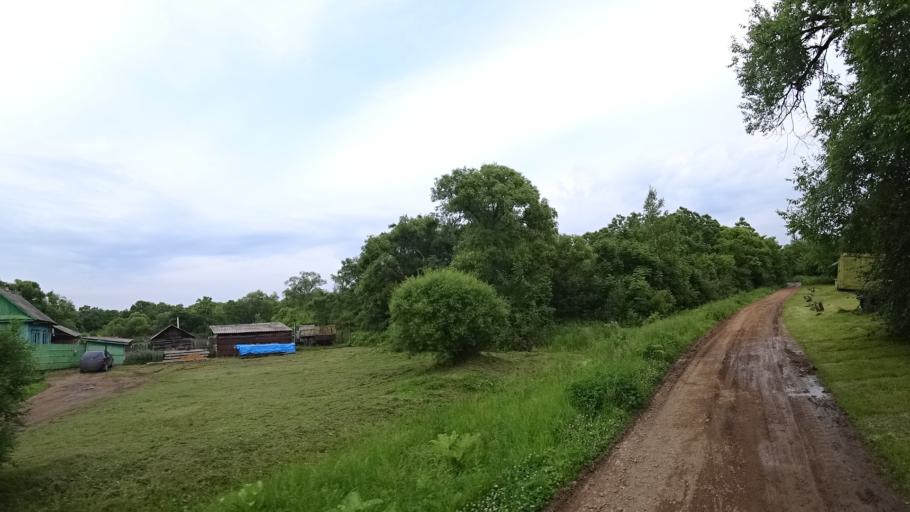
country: RU
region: Primorskiy
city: Novosysoyevka
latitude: 44.2396
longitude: 133.3780
